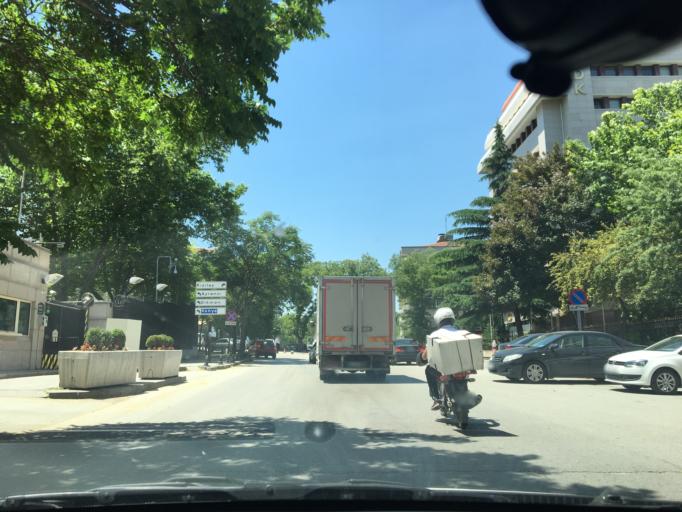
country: TR
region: Ankara
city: Ankara
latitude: 39.9086
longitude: 32.8556
